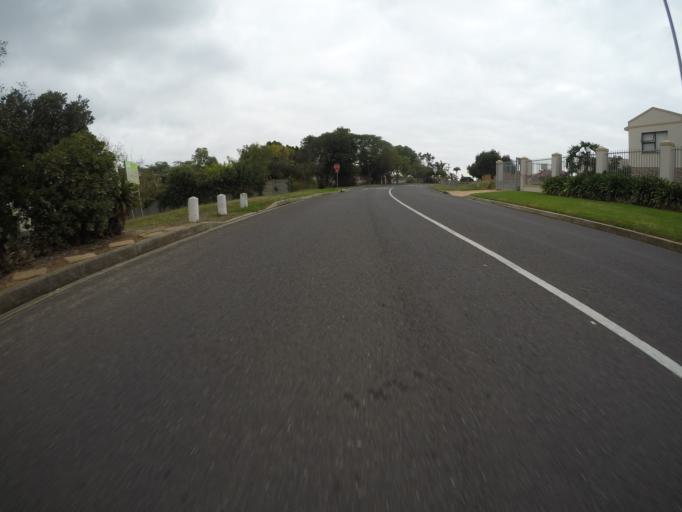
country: ZA
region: Western Cape
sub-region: City of Cape Town
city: Kraaifontein
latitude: -33.8676
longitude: 18.6494
